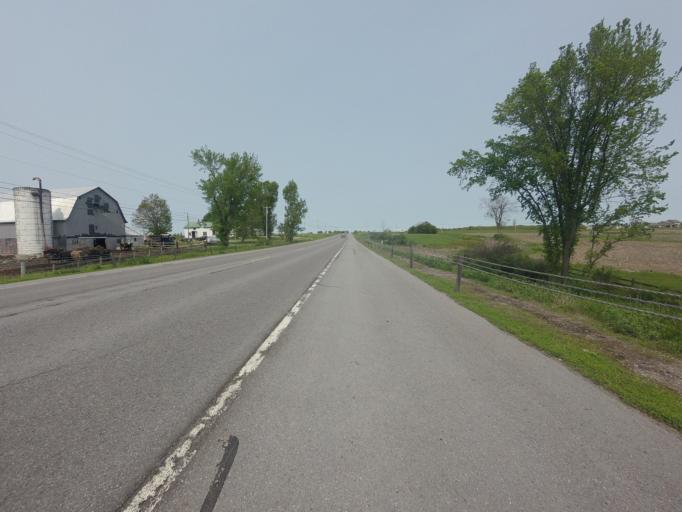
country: US
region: New York
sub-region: Jefferson County
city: Dexter
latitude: 44.0529
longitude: -76.1037
